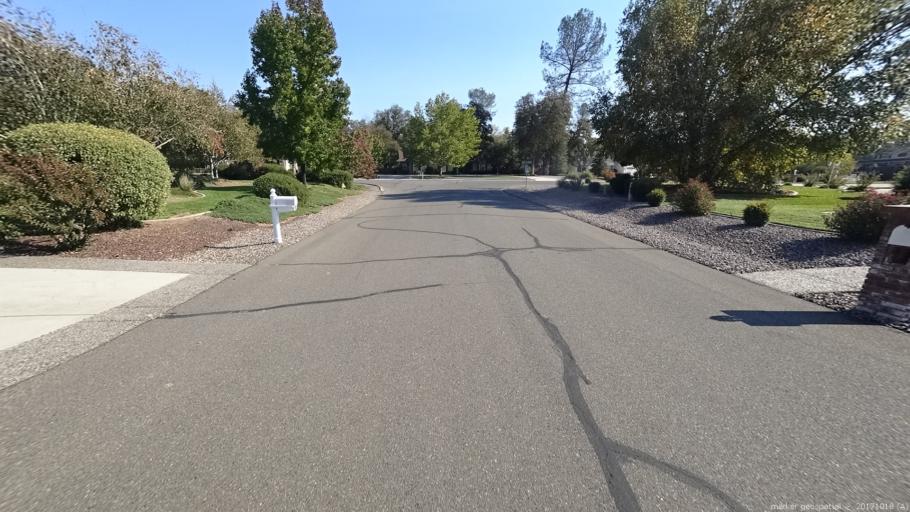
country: US
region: California
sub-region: Shasta County
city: Palo Cedro
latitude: 40.5587
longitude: -122.2335
